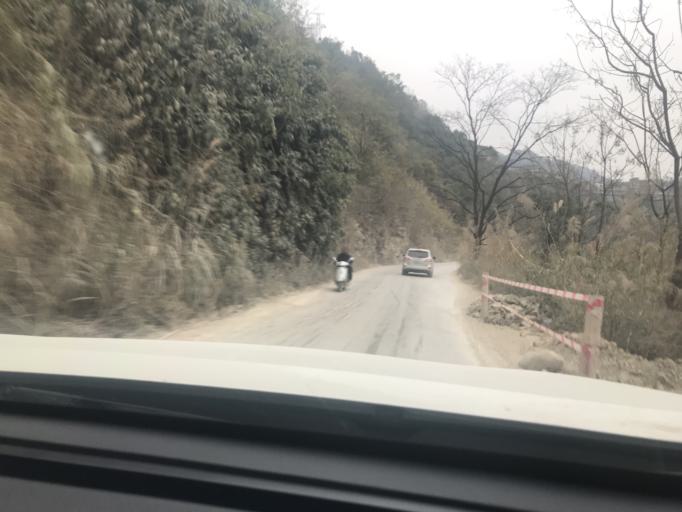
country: CN
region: Guangxi Zhuangzu Zizhiqu
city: Xinzhou
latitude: 24.9898
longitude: 105.8240
